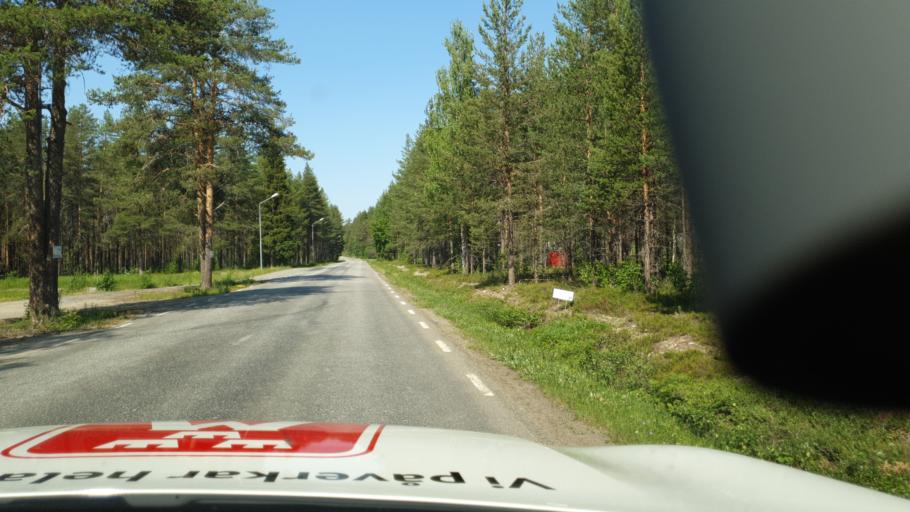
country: SE
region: Vaesterbotten
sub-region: Skelleftea Kommun
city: Langsele
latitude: 64.9550
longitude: 19.9153
